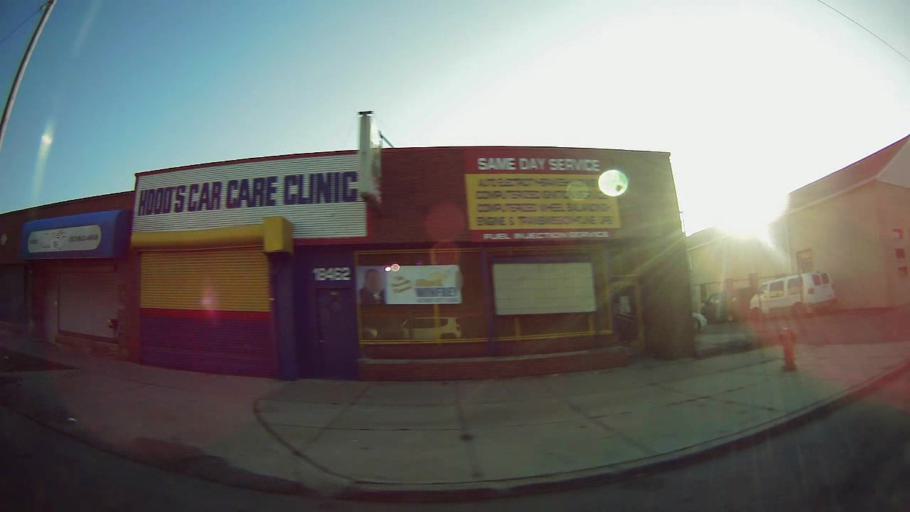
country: US
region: Michigan
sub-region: Oakland County
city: Oak Park
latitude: 42.4270
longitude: -83.1608
